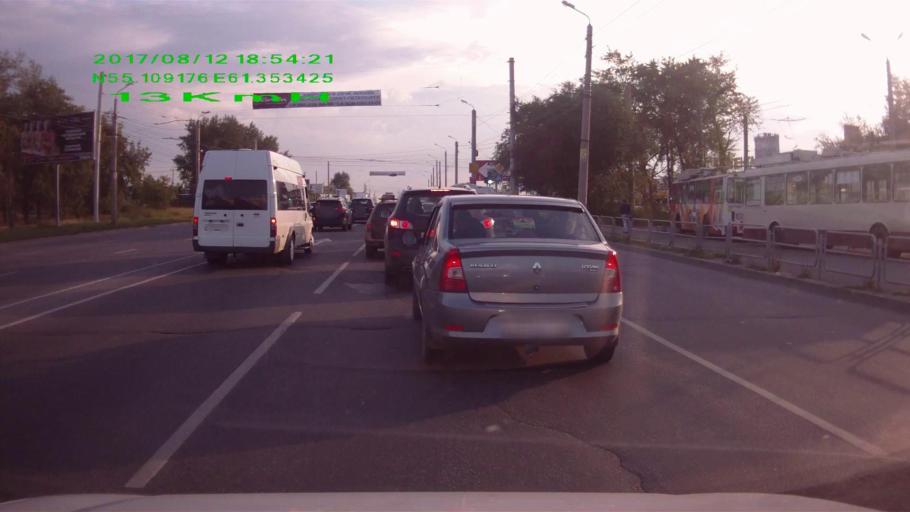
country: RU
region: Chelyabinsk
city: Novosineglazovskiy
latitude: 55.1062
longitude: 61.3487
